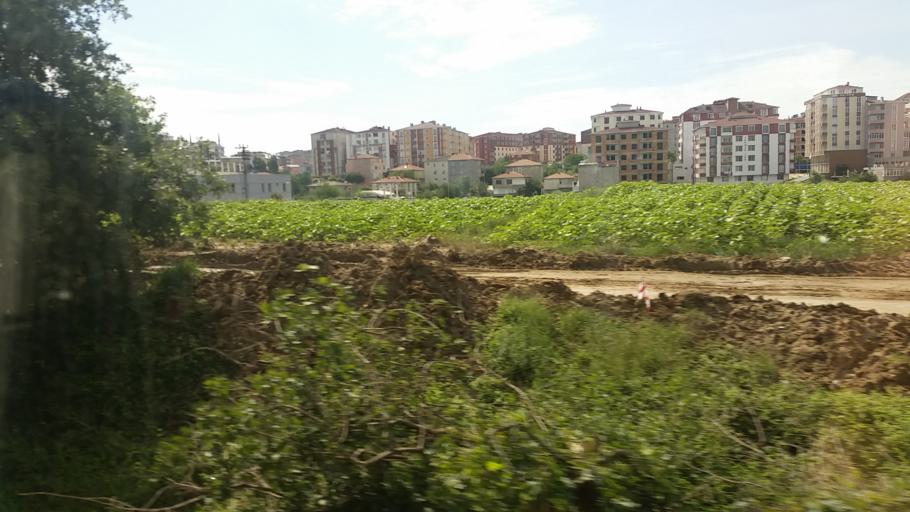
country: TR
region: Tekirdag
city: Cerkezkoey
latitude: 41.2717
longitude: 27.9589
